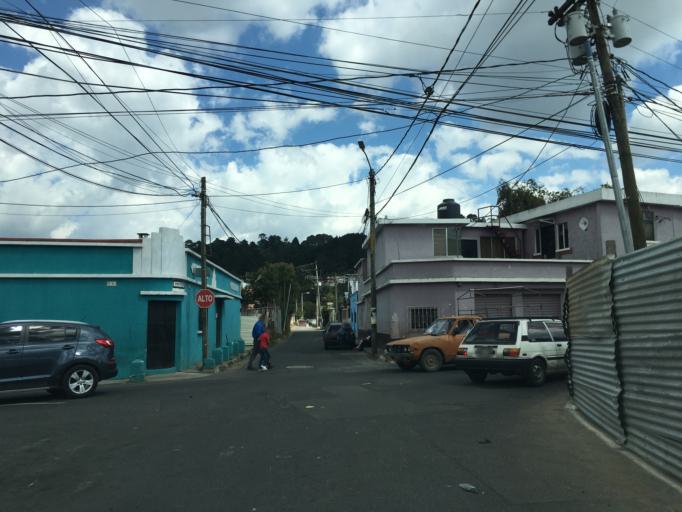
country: GT
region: Guatemala
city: San Jose Pinula
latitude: 14.5727
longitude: -90.4445
